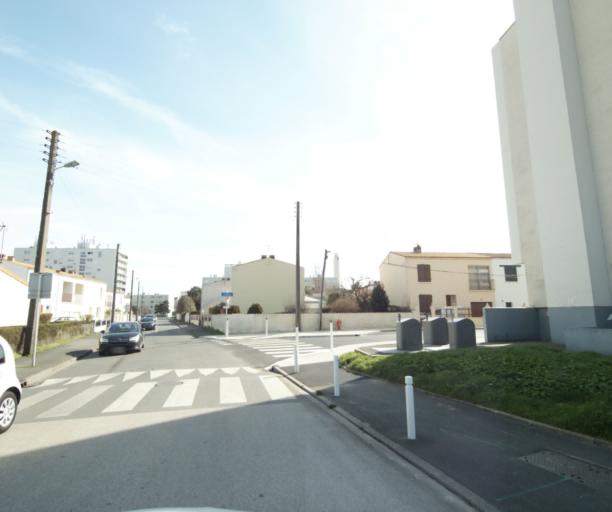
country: FR
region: Poitou-Charentes
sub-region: Departement de la Charente-Maritime
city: La Rochelle
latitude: 46.1709
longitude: -1.1737
